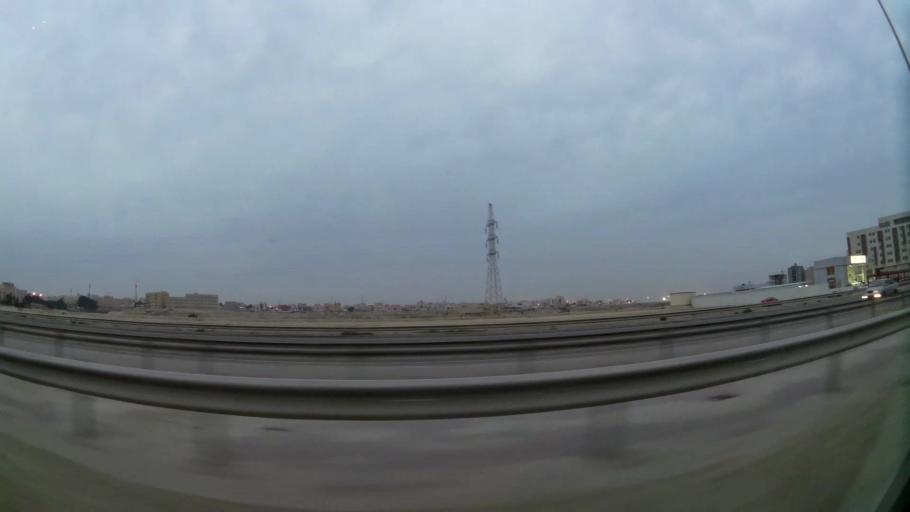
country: BH
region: Northern
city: Ar Rifa'
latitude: 26.1467
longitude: 50.5766
